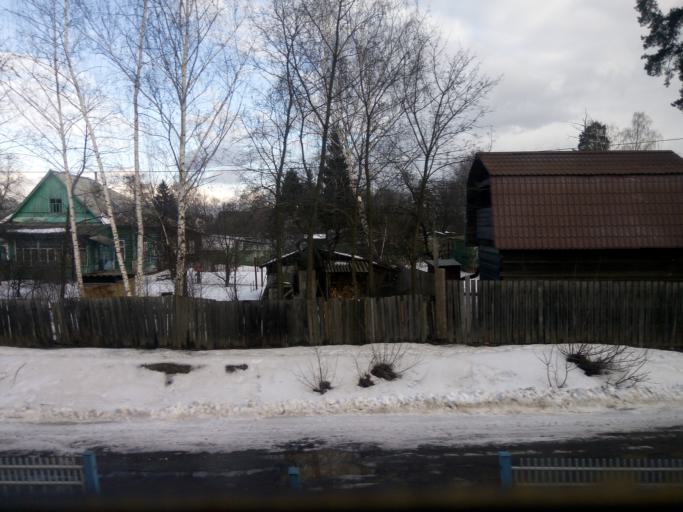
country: RU
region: Moskovskaya
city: Cherkizovo
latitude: 55.9607
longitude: 37.8052
